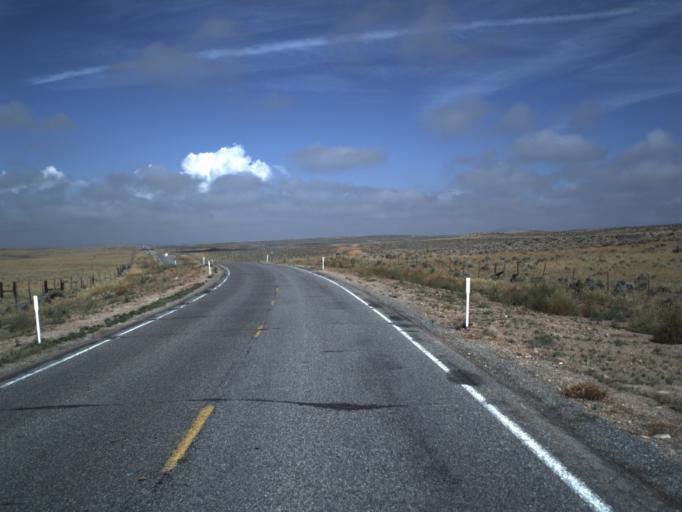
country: US
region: Wyoming
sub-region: Uinta County
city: Evanston
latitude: 41.4254
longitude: -111.0539
